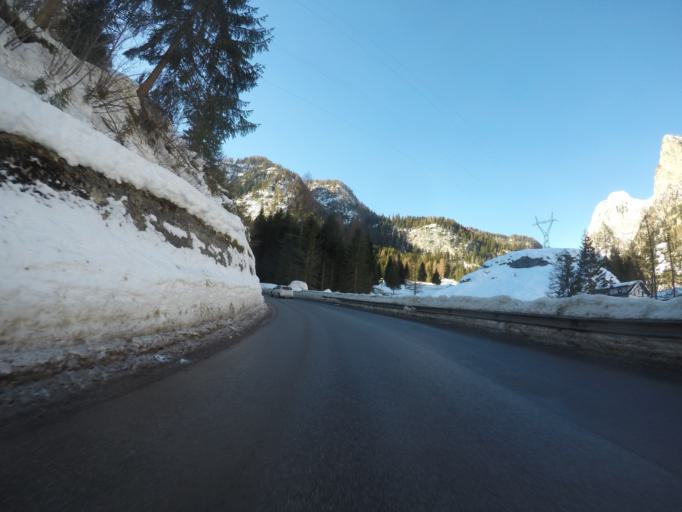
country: IT
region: Veneto
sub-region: Provincia di Belluno
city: Rocca Pietore
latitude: 46.4234
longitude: 11.9376
